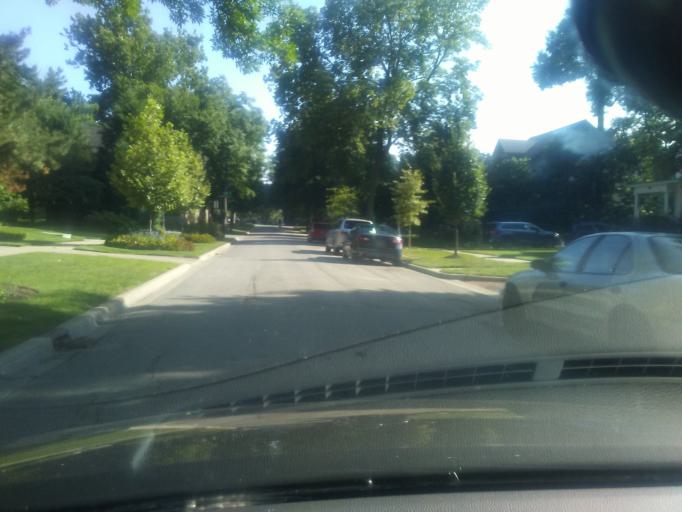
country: US
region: Illinois
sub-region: Cook County
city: Evanston
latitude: 42.0469
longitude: -87.6937
